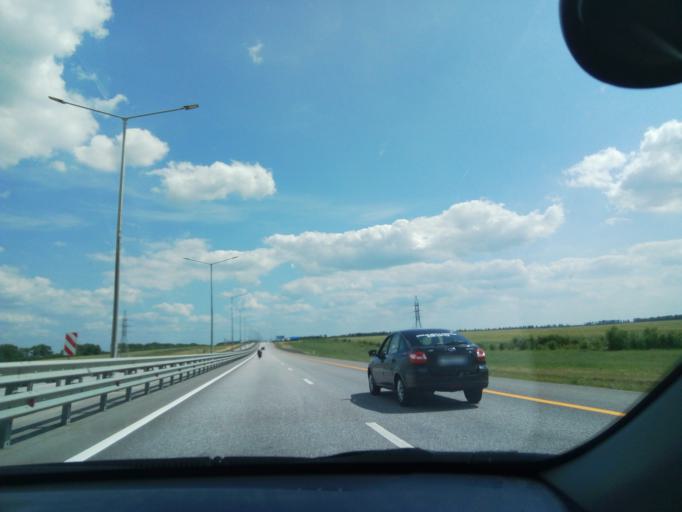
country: RU
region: Voronezj
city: Podkletnoye
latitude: 51.5475
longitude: 39.4946
